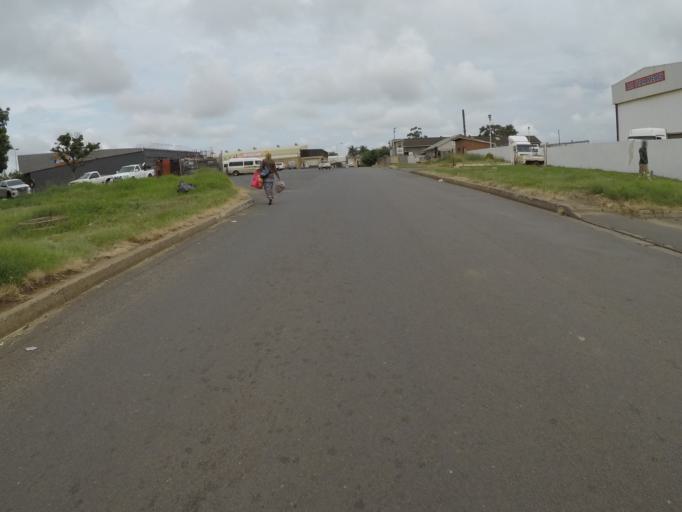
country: ZA
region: KwaZulu-Natal
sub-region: uThungulu District Municipality
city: Empangeni
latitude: -28.7747
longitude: 31.9019
